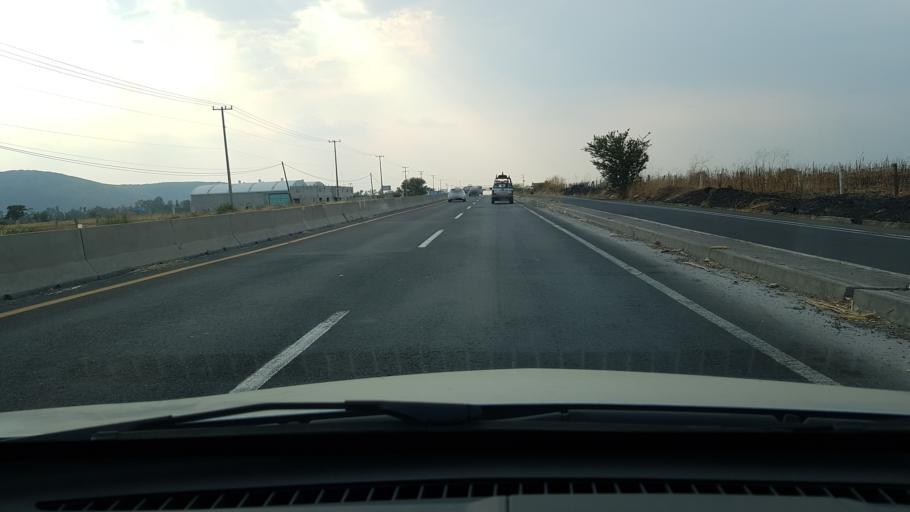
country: MX
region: Morelos
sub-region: Ayala
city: Unidad Habitacional Mariano Matamoros
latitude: 18.7415
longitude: -98.8329
